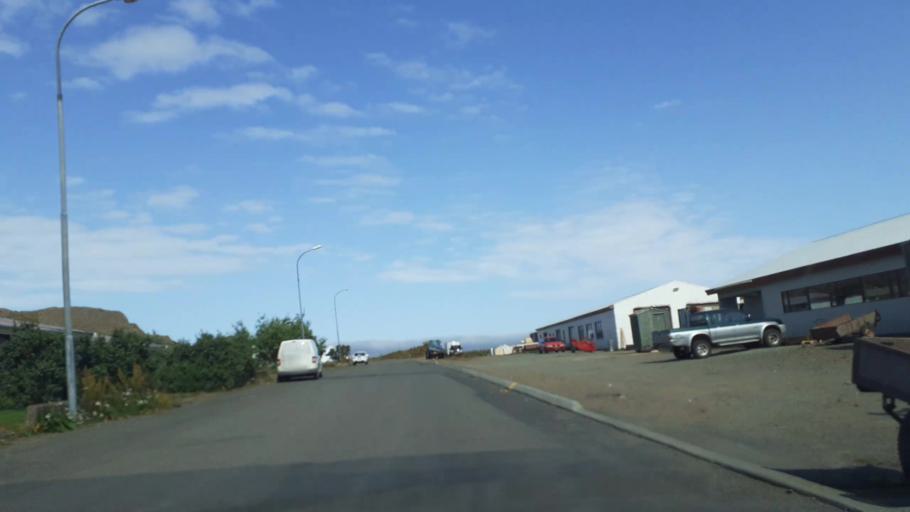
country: IS
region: Northwest
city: Saudarkrokur
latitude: 65.8277
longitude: -20.3164
